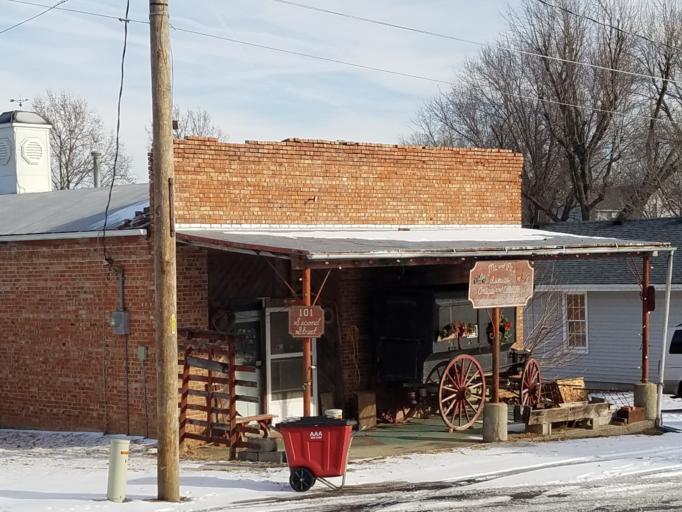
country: US
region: Missouri
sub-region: Ray County
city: Albany
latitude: 39.1306
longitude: -94.0749
